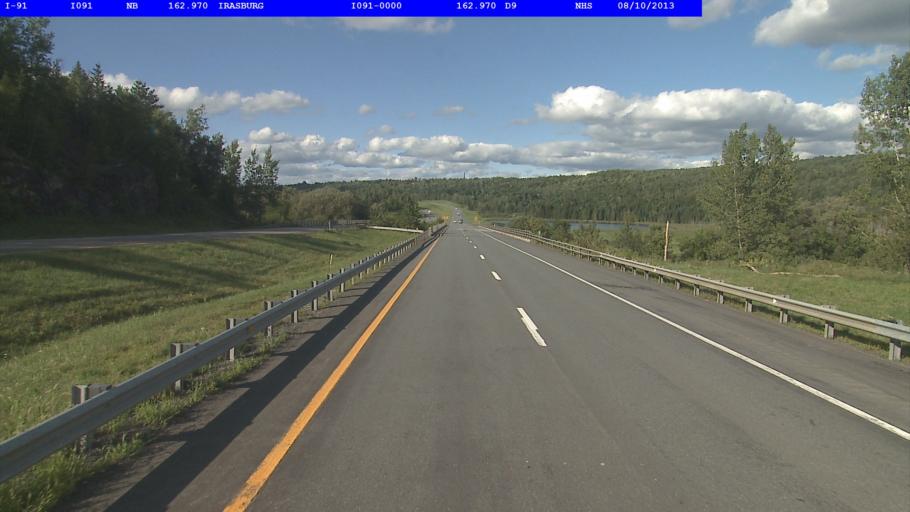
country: US
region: Vermont
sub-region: Orleans County
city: Newport
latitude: 44.8275
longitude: -72.2027
